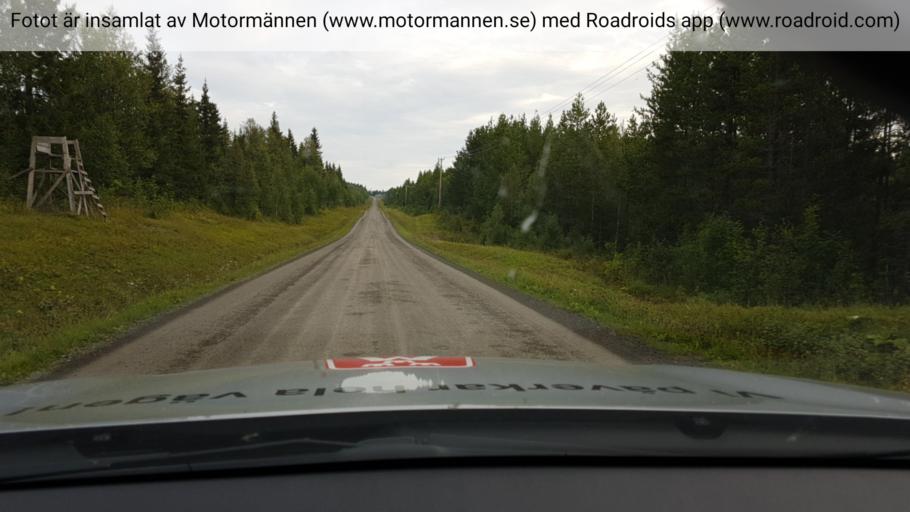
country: SE
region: Jaemtland
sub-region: OEstersunds Kommun
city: Lit
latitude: 63.6253
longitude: 14.9750
